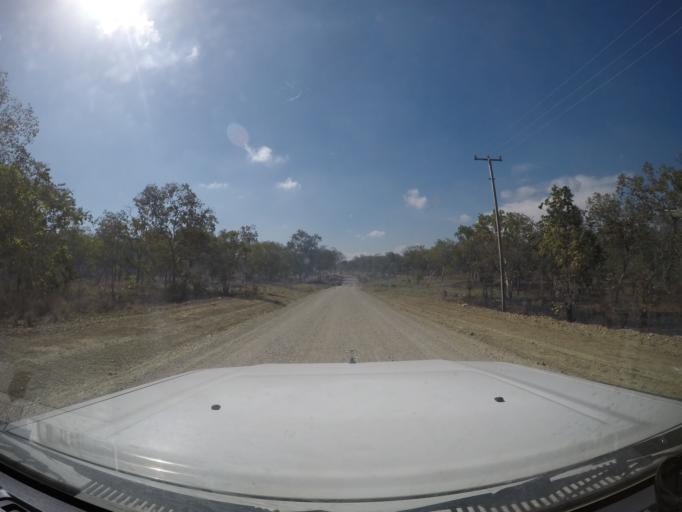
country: PG
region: Central Province
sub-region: Rigo
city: Kwikila
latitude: -9.9646
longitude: 147.6597
